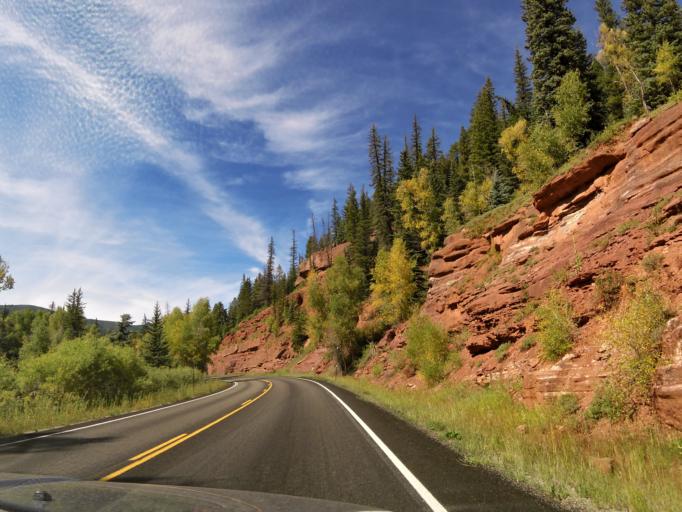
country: US
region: Colorado
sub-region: Montezuma County
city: Mancos
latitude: 37.6048
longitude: -108.1068
